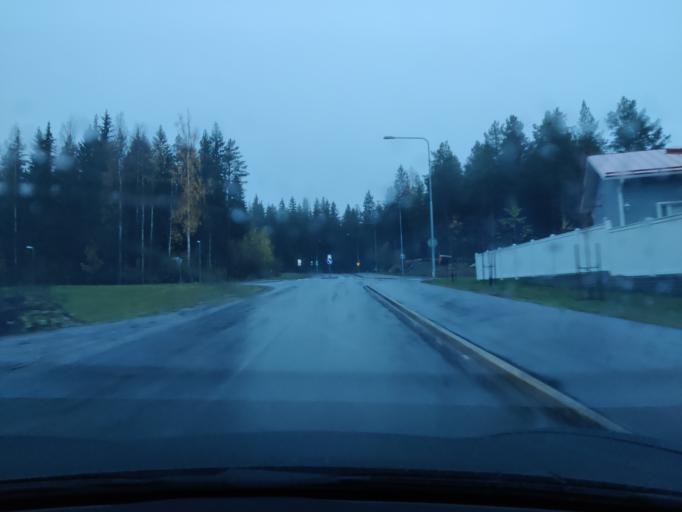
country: FI
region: Northern Savo
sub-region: Kuopio
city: Kuopio
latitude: 62.8320
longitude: 27.7144
